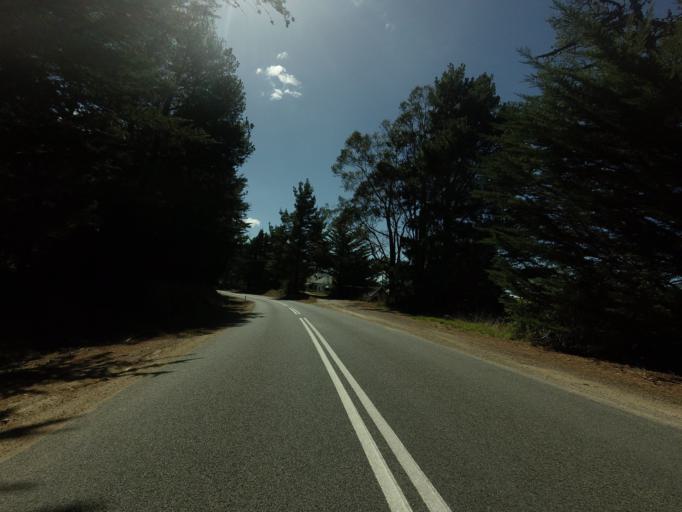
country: AU
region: Tasmania
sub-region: Break O'Day
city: St Helens
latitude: -41.6679
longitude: 148.2846
